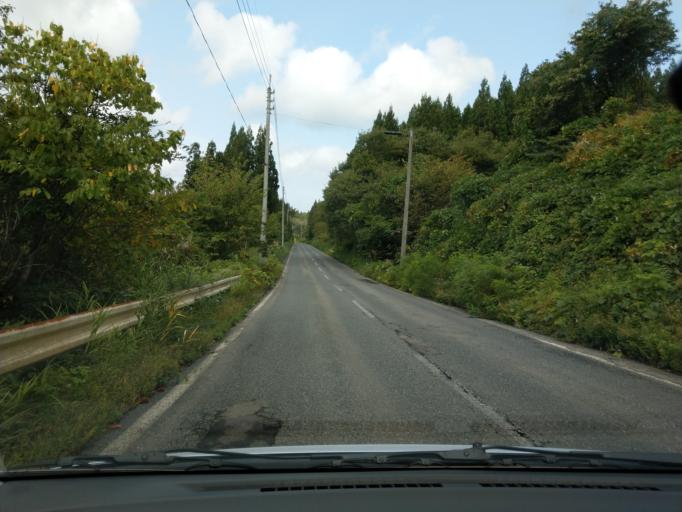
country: JP
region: Akita
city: Omagari
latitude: 39.4592
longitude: 140.3195
